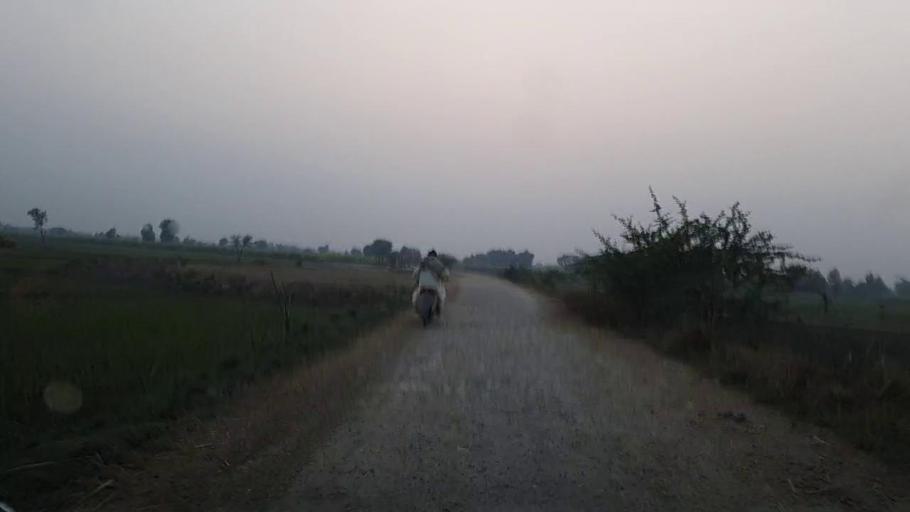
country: PK
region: Sindh
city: Kandiari
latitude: 26.9748
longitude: 68.4791
